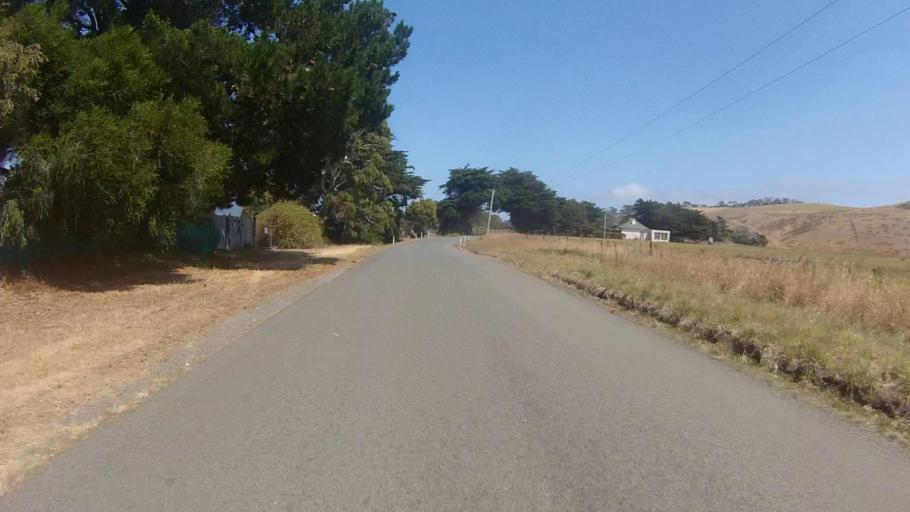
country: AU
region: Tasmania
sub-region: Sorell
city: Sorell
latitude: -42.8280
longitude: 147.8585
